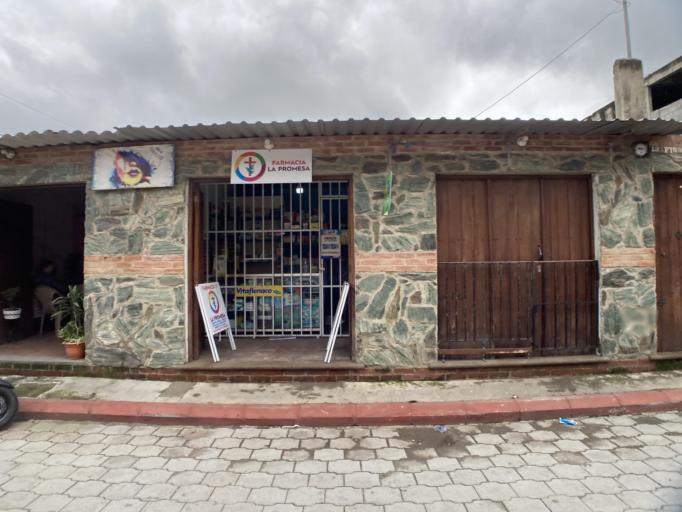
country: GT
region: Sacatepequez
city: Jocotenango
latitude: 14.5801
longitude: -90.7474
